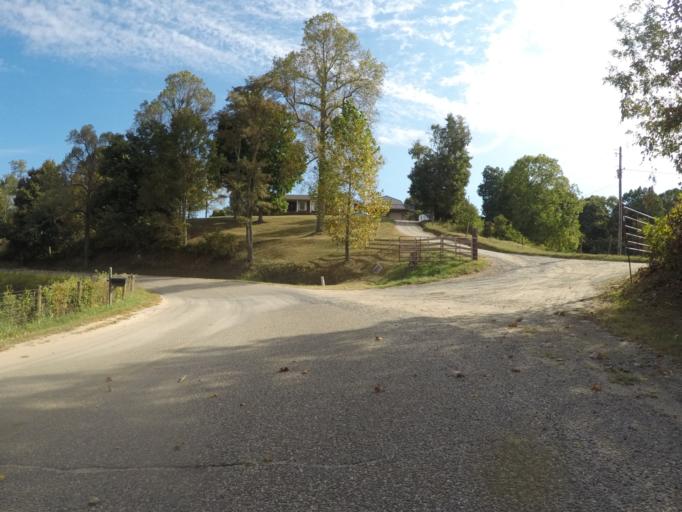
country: US
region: West Virginia
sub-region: Cabell County
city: Lesage
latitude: 38.5833
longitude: -82.4250
